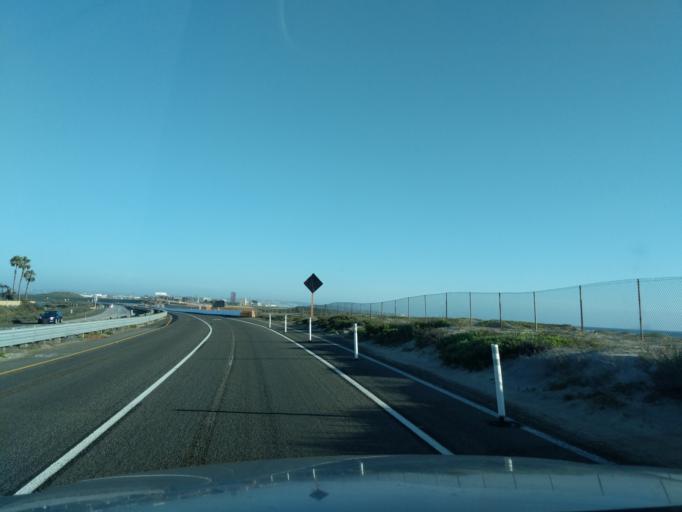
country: US
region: California
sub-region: San Diego County
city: Imperial Beach
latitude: 32.6121
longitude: -117.1344
